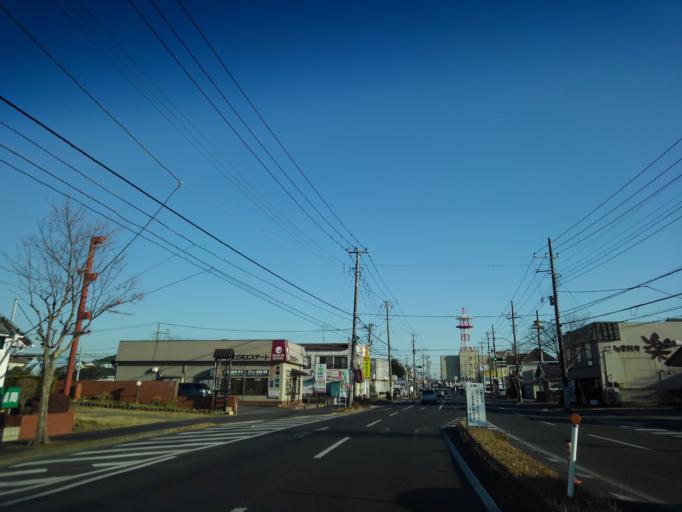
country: JP
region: Chiba
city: Kimitsu
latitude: 35.3285
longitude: 139.9036
